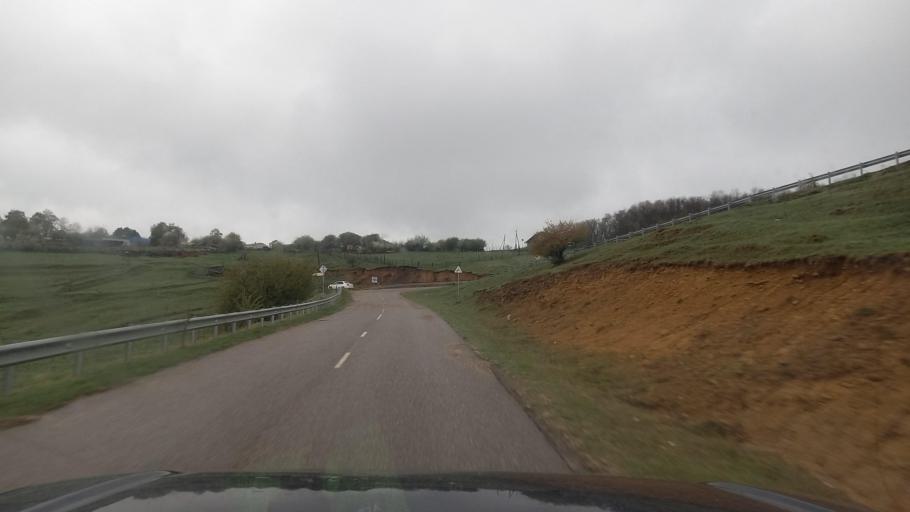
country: RU
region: Stavropol'skiy
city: Nezhinskiy
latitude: 43.8622
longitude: 42.6527
